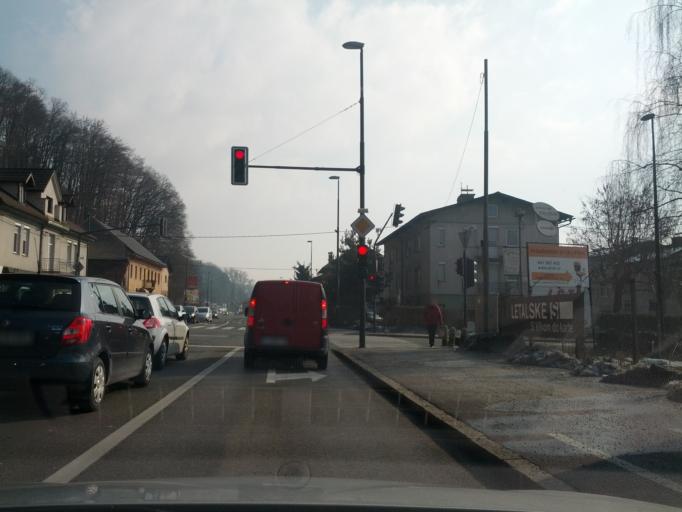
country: SI
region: Ljubljana
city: Ljubljana
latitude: 46.0303
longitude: 14.5319
